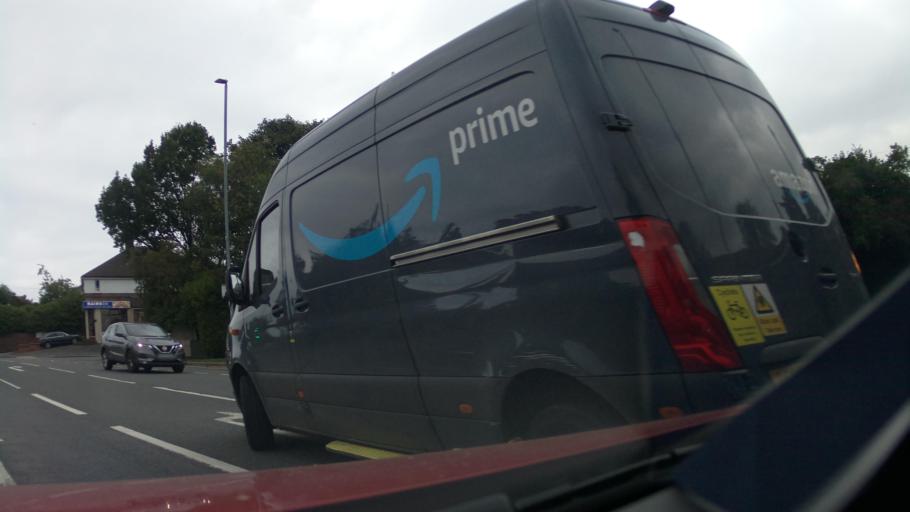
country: GB
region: England
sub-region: Staffordshire
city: Longton
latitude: 53.0221
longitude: -2.1242
